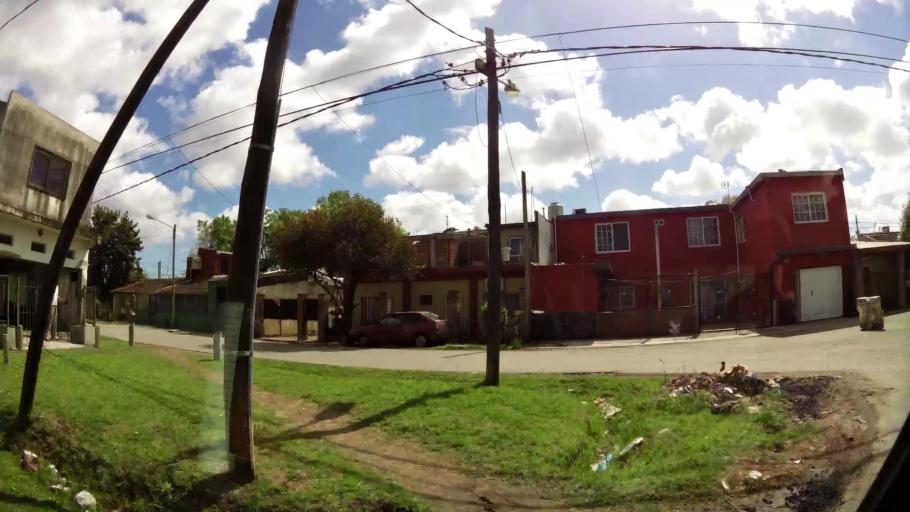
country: AR
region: Buenos Aires
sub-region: Partido de Quilmes
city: Quilmes
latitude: -34.8251
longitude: -58.1875
